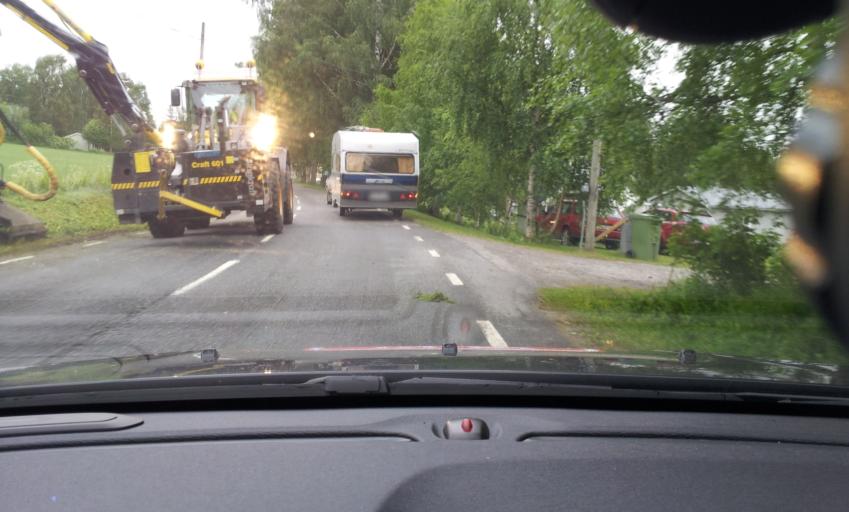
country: SE
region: Jaemtland
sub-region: Ragunda Kommun
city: Hammarstrand
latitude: 63.2147
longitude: 15.9486
